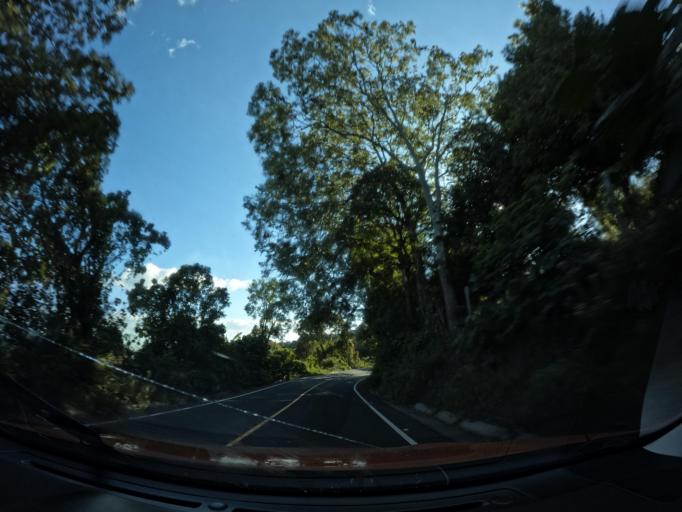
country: GT
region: Escuintla
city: Palin
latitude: 14.4549
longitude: -90.6944
